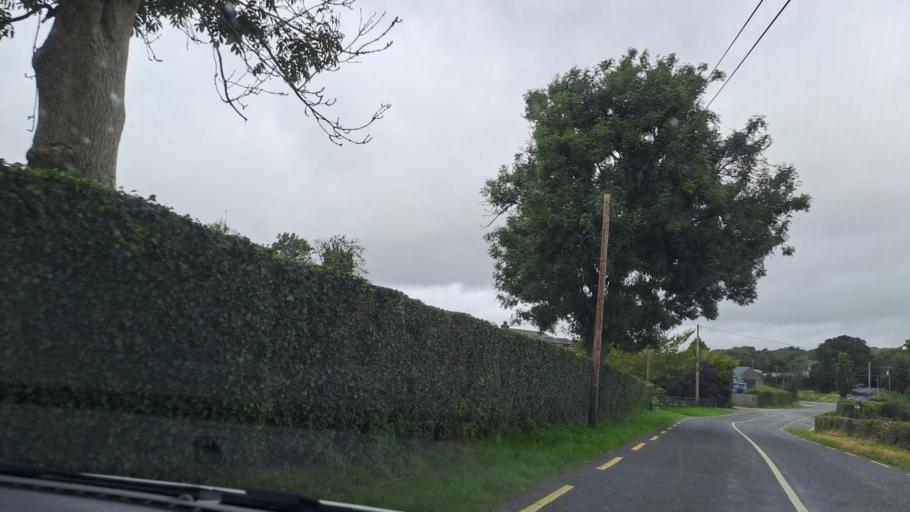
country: IE
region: Ulster
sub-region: County Monaghan
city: Carrickmacross
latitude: 54.0207
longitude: -6.7120
